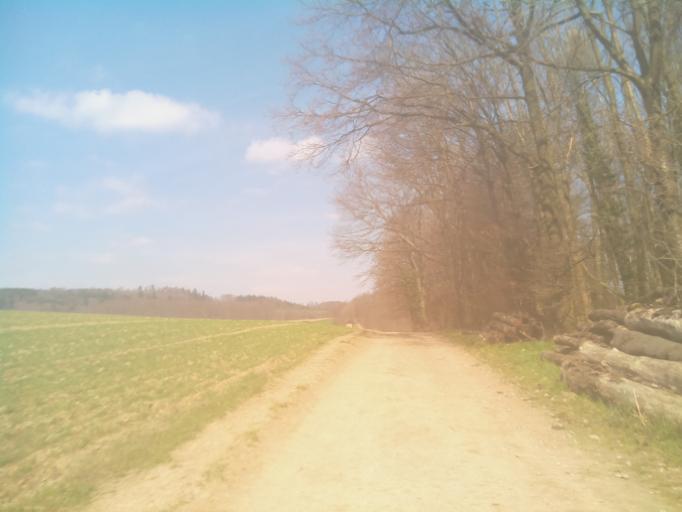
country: DE
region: Hesse
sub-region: Regierungsbezirk Darmstadt
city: Morlenbach
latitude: 49.6034
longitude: 8.7124
